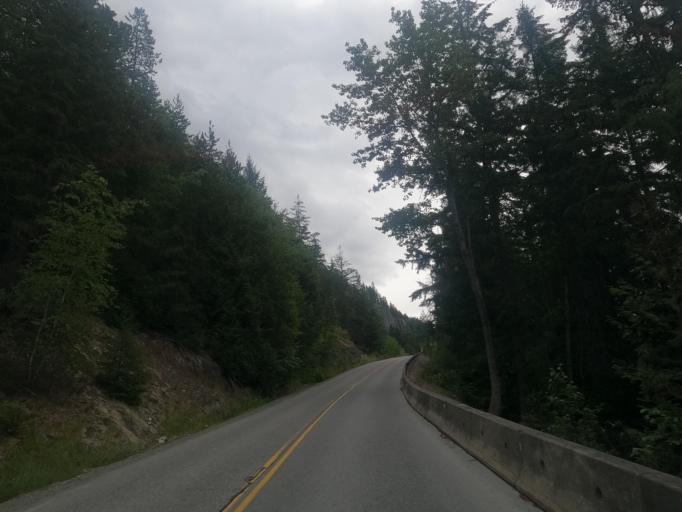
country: CA
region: British Columbia
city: Pemberton
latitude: 50.3008
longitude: -122.5853
